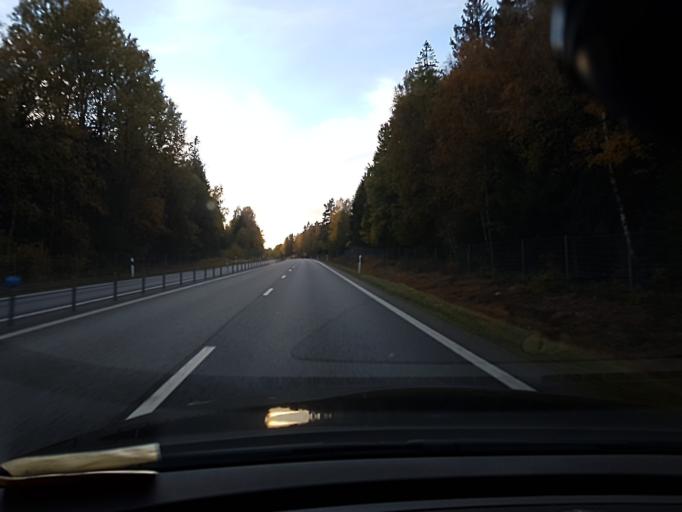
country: SE
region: Kronoberg
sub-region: Ljungby Kommun
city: Lagan
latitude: 56.8518
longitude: 14.0166
